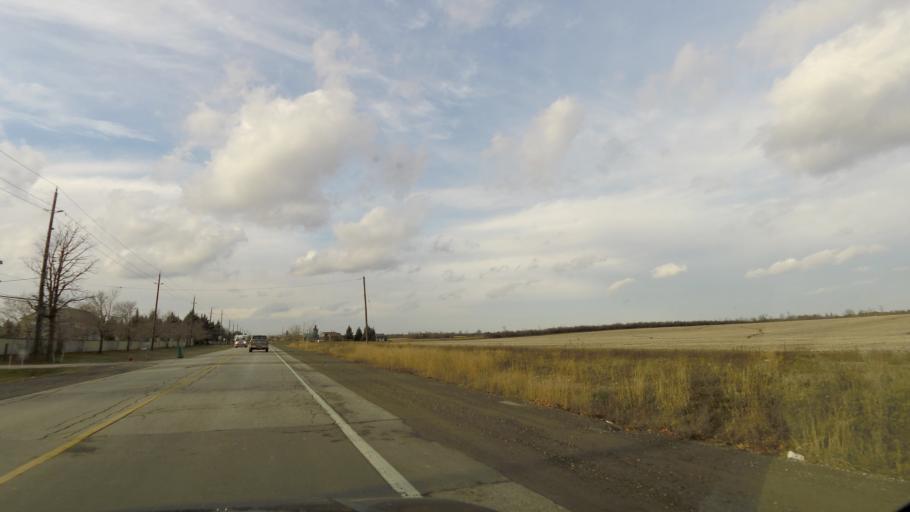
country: CA
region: Ontario
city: Brampton
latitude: 43.8014
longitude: -79.7029
